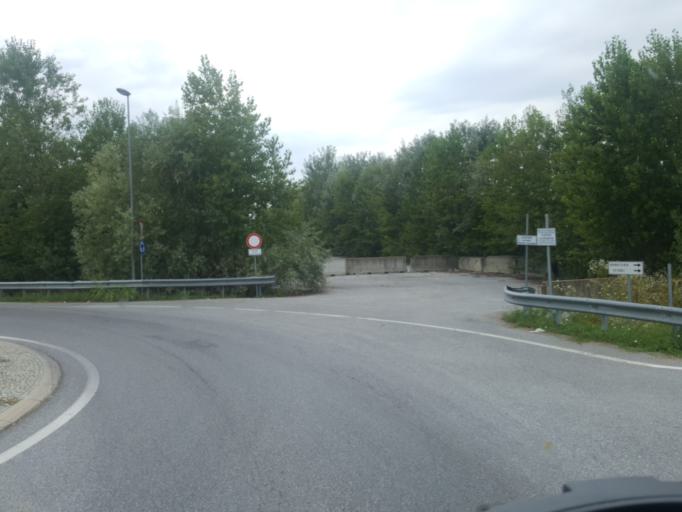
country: IT
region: Piedmont
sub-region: Provincia di Cuneo
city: Briaglia
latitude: 44.4241
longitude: 7.8515
